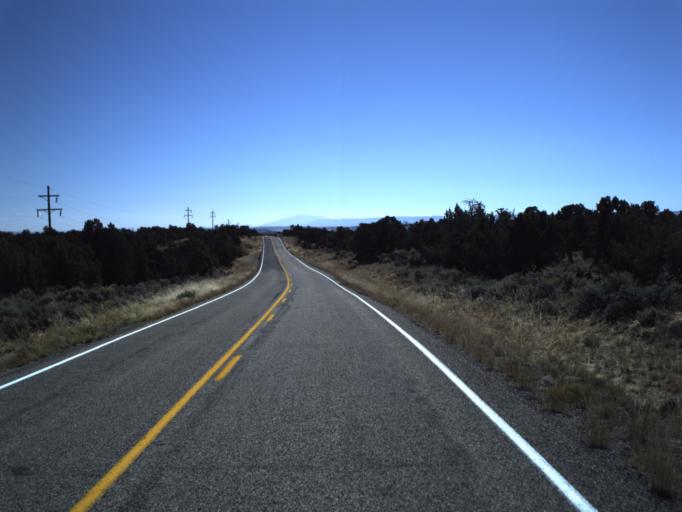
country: US
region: Utah
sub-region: Wayne County
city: Loa
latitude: 37.8633
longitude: -111.4395
